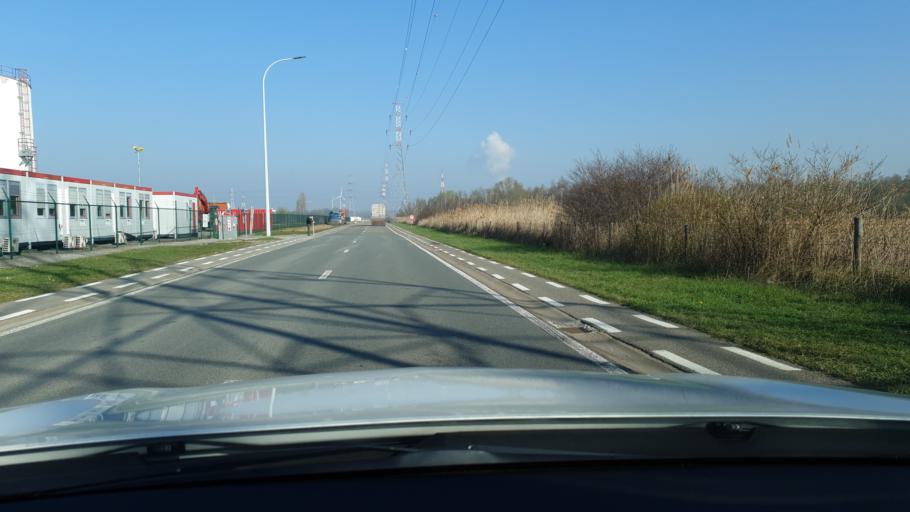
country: BE
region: Flanders
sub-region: Provincie Antwerpen
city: Zwijndrecht
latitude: 51.2414
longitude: 4.2908
